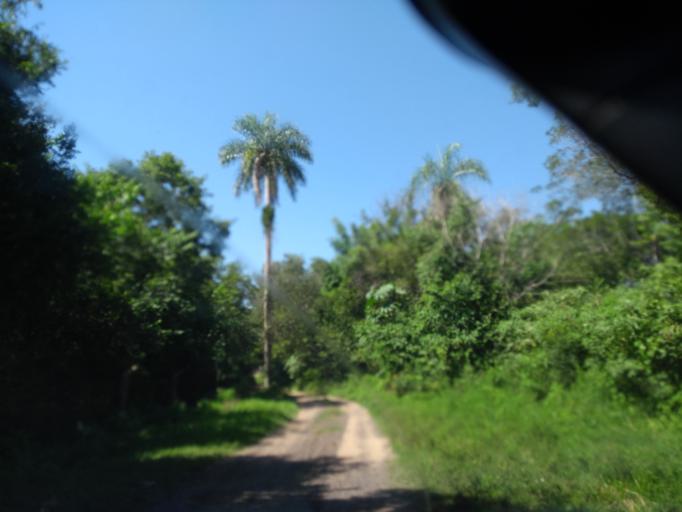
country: AR
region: Chaco
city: Resistencia
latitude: -27.4273
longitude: -58.9513
